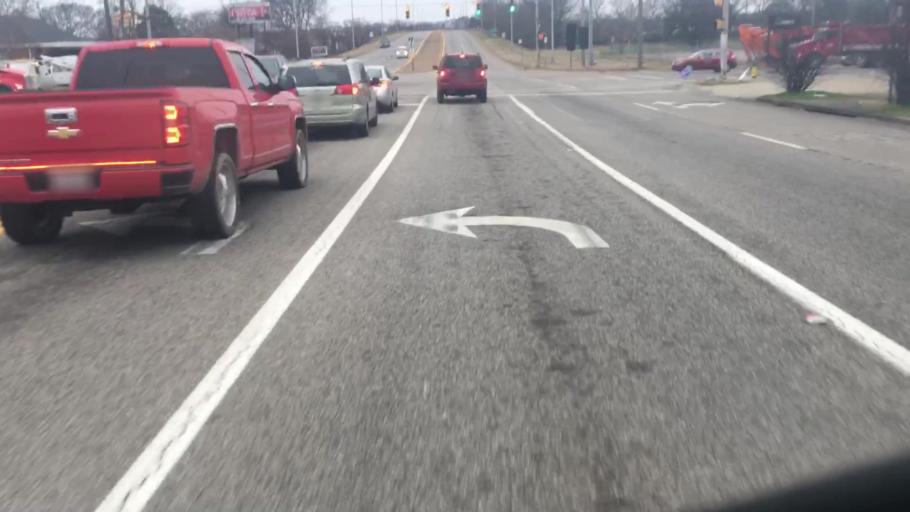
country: US
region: Alabama
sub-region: Jefferson County
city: Birmingham
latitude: 33.5456
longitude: -86.8153
